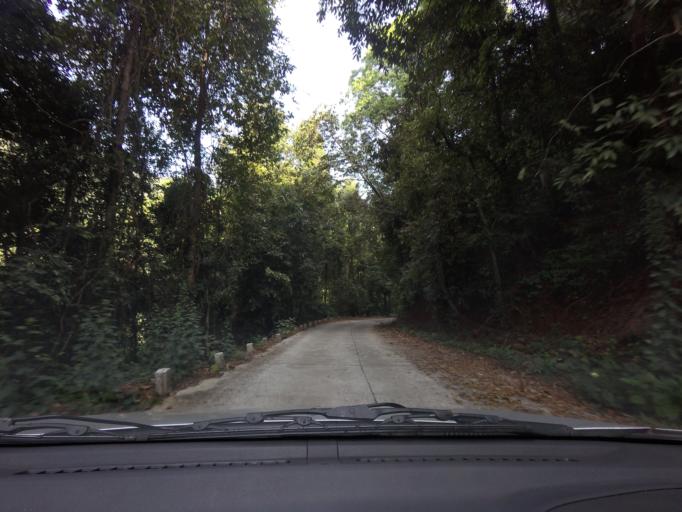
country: IN
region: Karnataka
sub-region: Kodagu
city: Sanivarsante
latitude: 12.7300
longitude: 75.6609
